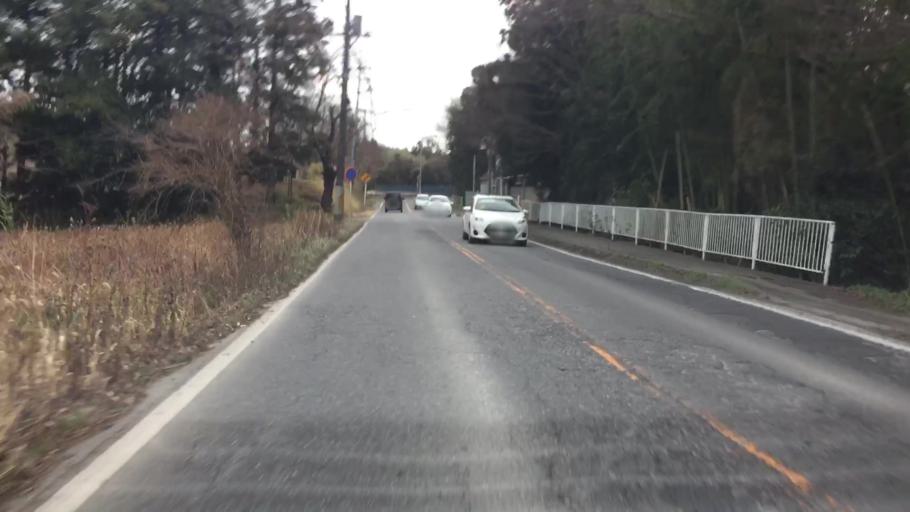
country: JP
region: Ibaraki
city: Ryugasaki
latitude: 35.8291
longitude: 140.1602
